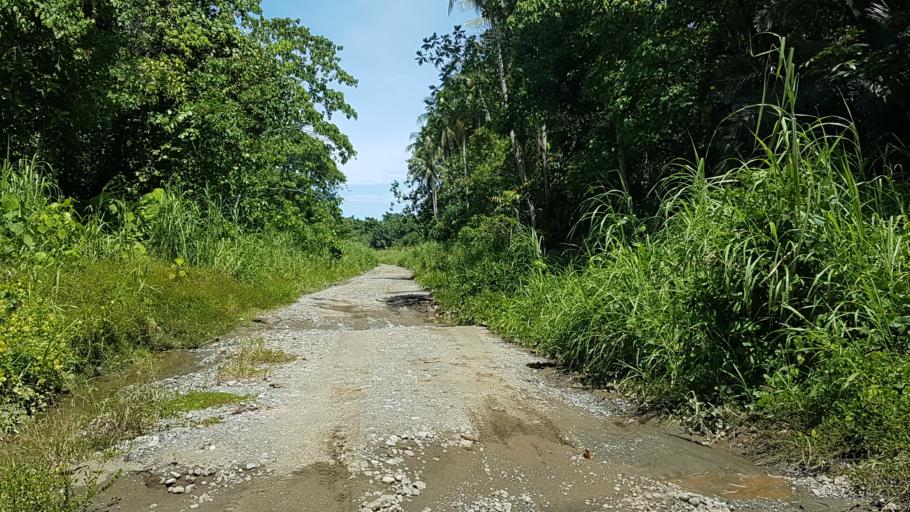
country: PG
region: Sandaun
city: Aitape
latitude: -3.2420
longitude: 142.5410
